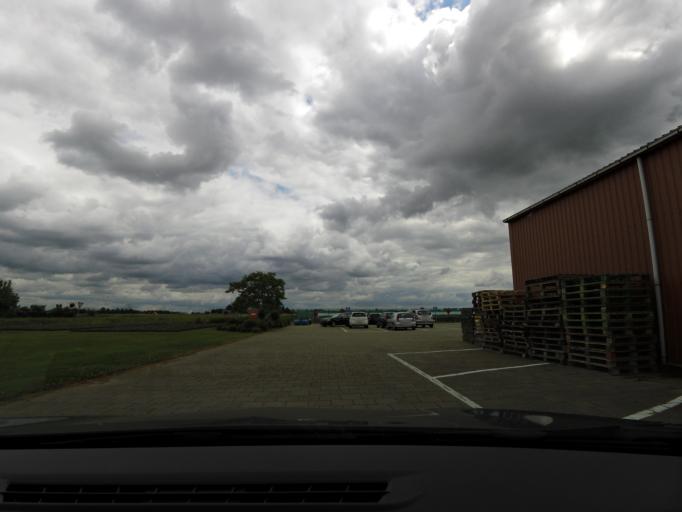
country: NL
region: South Holland
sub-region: Gemeente Binnenmaas
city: Mijnsheerenland
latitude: 51.8050
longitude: 4.5019
